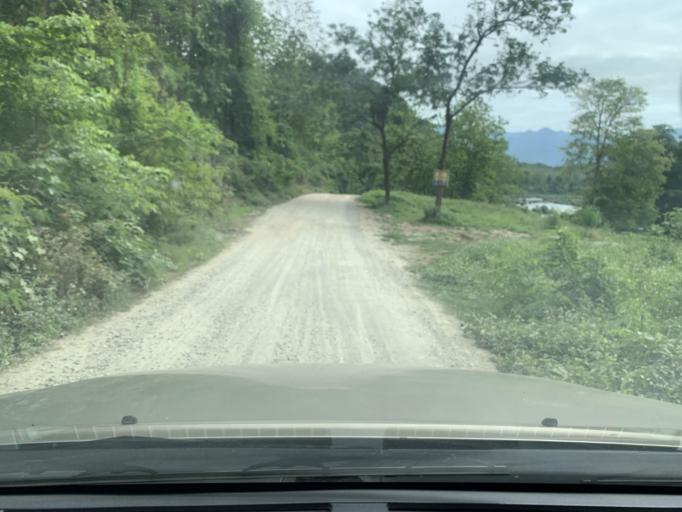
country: LA
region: Louangphabang
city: Louangphabang
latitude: 19.8864
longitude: 102.1893
